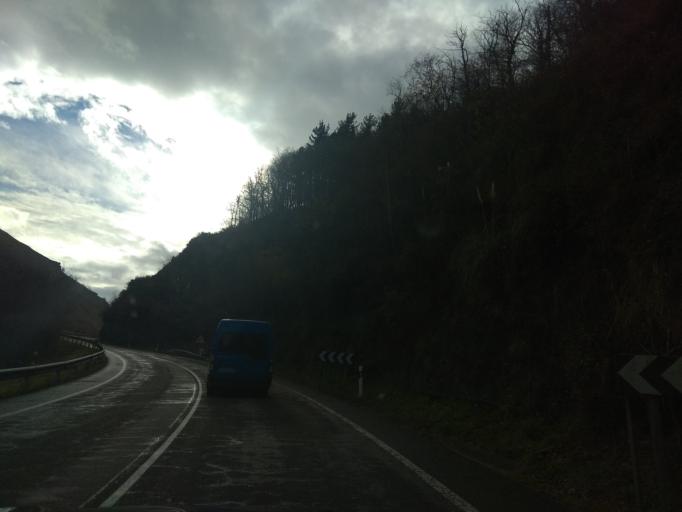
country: ES
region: Cantabria
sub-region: Provincia de Cantabria
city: San Pedro del Romeral
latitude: 43.1423
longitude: -3.9001
